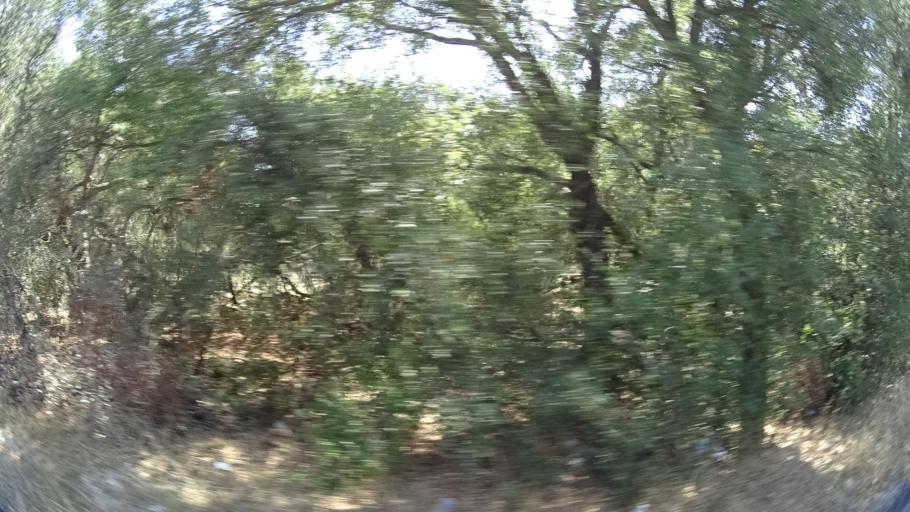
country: US
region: California
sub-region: San Diego County
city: Valley Center
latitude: 33.2455
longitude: -116.9916
